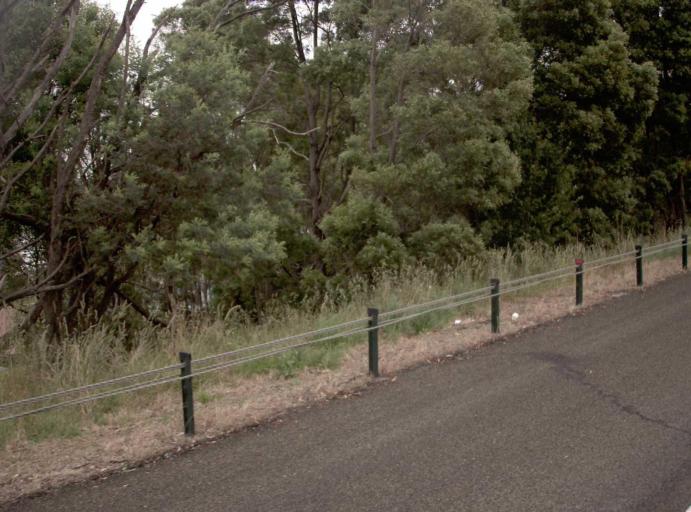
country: AU
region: Victoria
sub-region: Baw Baw
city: Warragul
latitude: -38.1680
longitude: 145.9163
